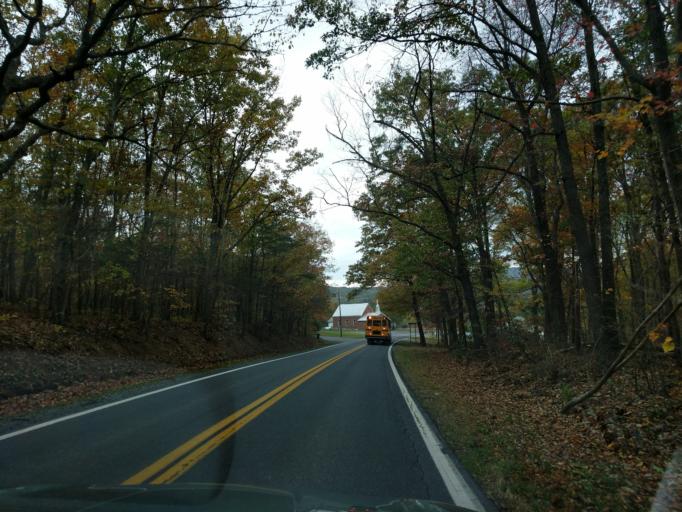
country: US
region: West Virginia
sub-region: Berkeley County
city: Inwood
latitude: 39.3918
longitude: -78.1855
